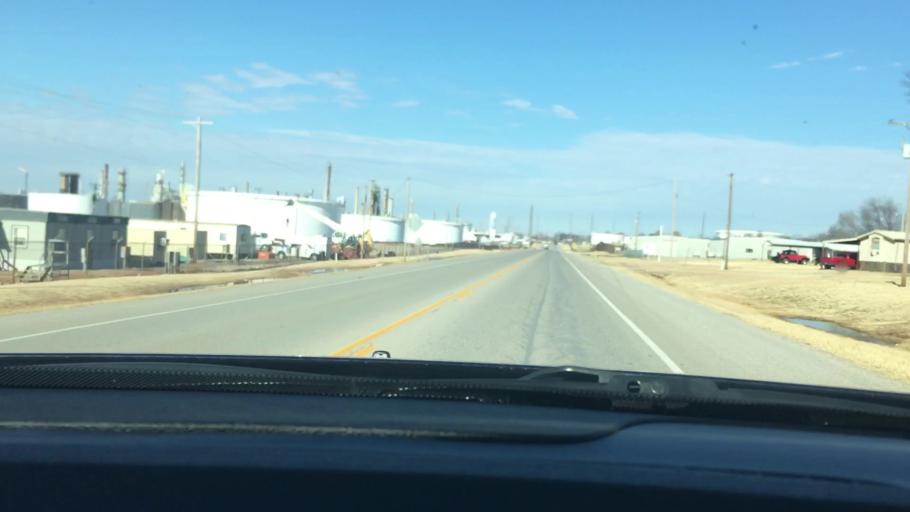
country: US
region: Oklahoma
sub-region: Garvin County
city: Wynnewood
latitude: 34.6259
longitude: -97.1637
